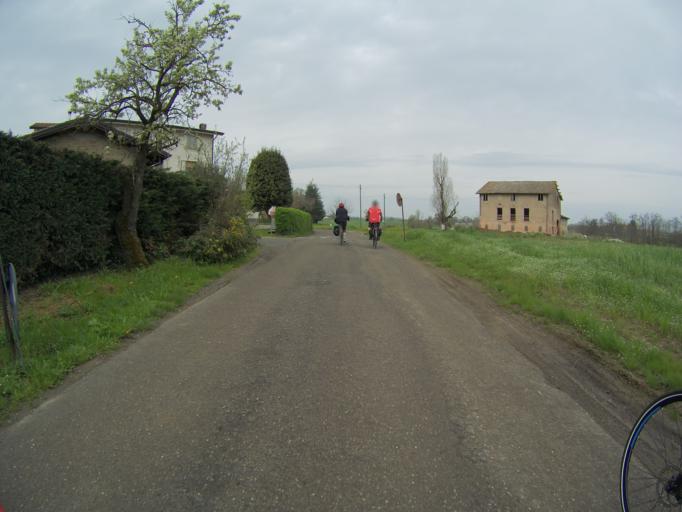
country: IT
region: Emilia-Romagna
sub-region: Provincia di Reggio Emilia
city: San Bartolomeo
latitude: 44.6663
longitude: 10.5606
